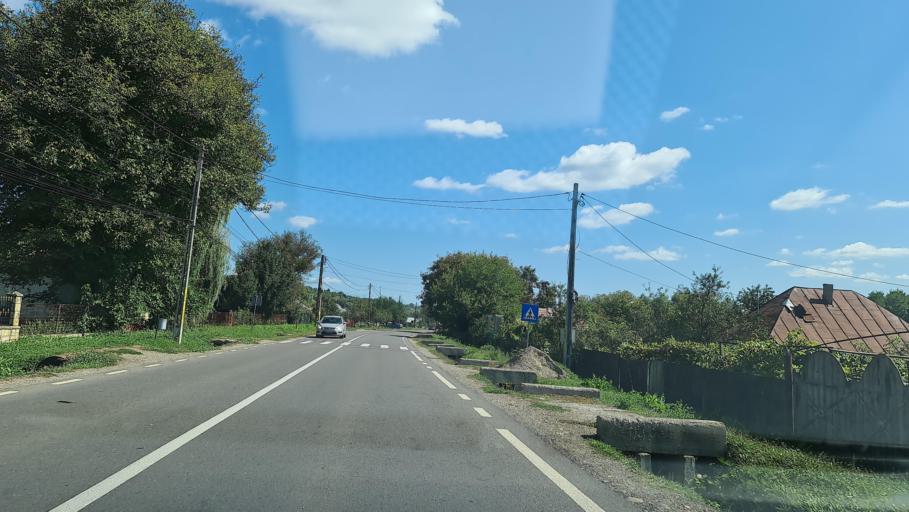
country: RO
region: Bacau
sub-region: Comuna Scorteni
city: Scorteni
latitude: 46.5321
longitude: 26.6296
